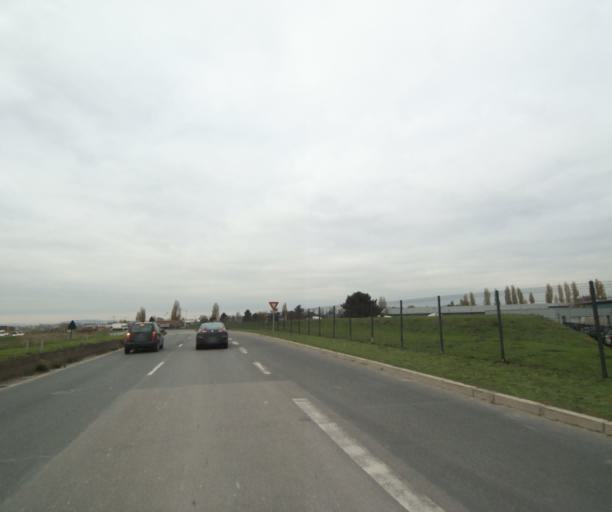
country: FR
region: Ile-de-France
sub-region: Departement du Val-d'Oise
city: Gonesse
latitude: 48.9759
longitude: 2.4588
